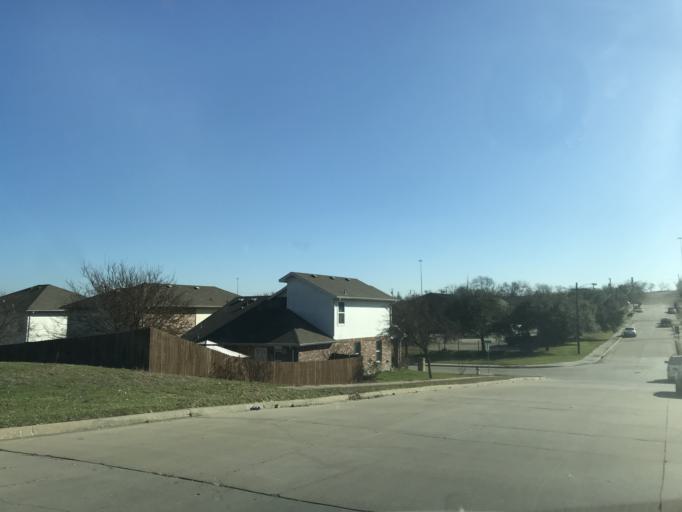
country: US
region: Texas
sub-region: Dallas County
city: Cockrell Hill
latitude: 32.7703
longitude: -96.9046
